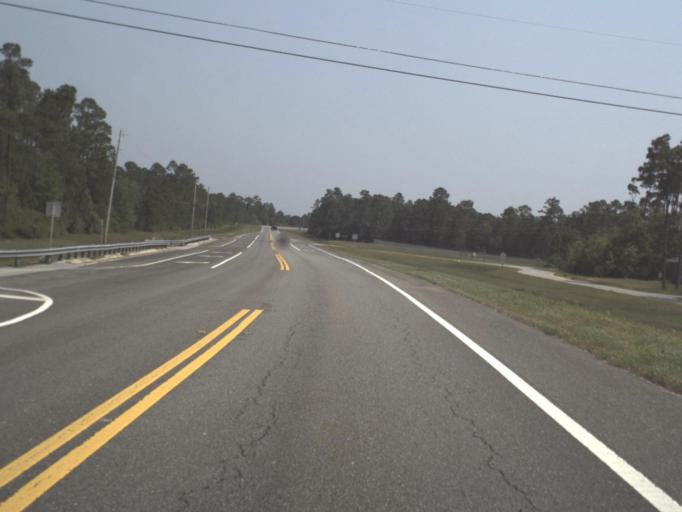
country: US
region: Florida
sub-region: Santa Rosa County
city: Bagdad
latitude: 30.5137
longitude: -87.0864
